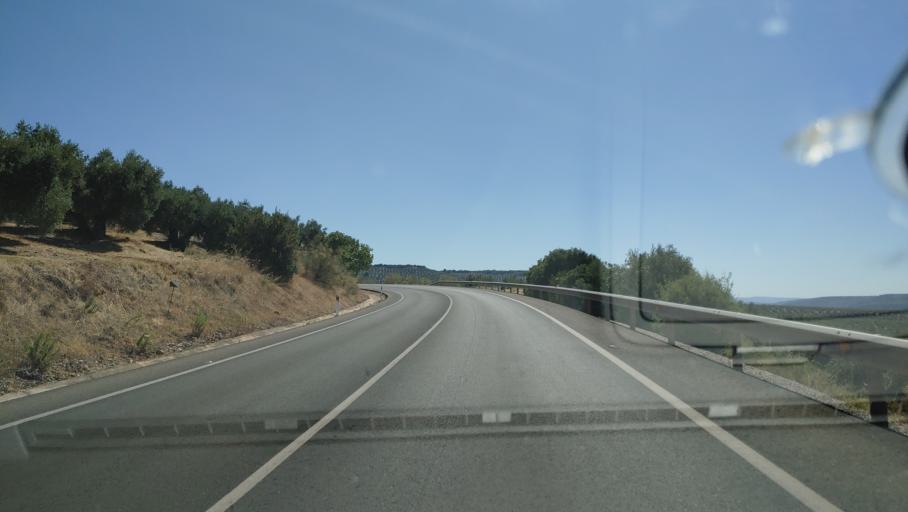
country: ES
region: Andalusia
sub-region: Provincia de Jaen
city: Campina
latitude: 38.2486
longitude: -2.9642
